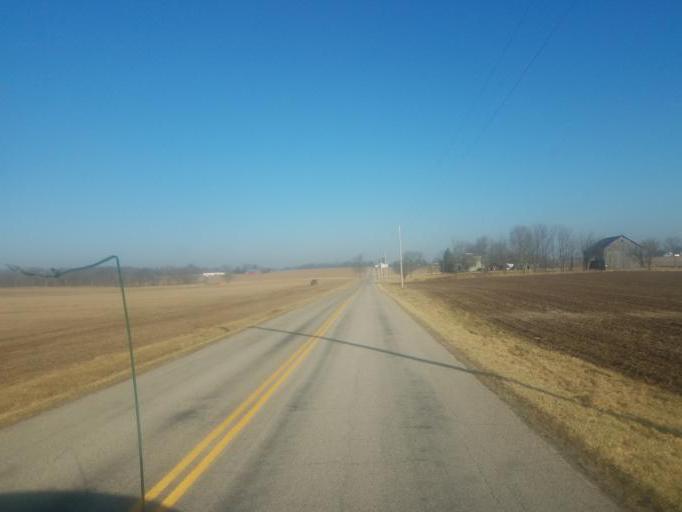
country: US
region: Ohio
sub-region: Crawford County
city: Bucyrus
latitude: 40.8897
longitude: -82.9400
